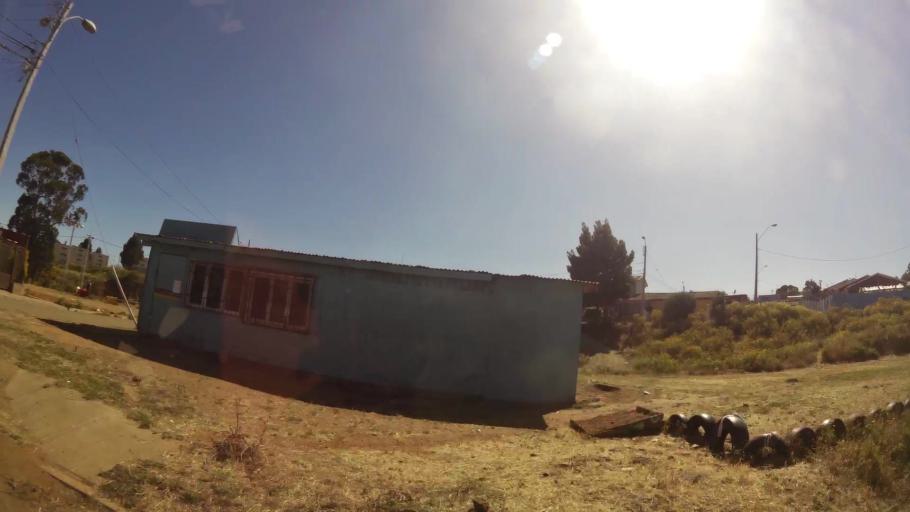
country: CL
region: Valparaiso
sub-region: Provincia de Valparaiso
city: Valparaiso
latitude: -33.0528
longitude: -71.6509
